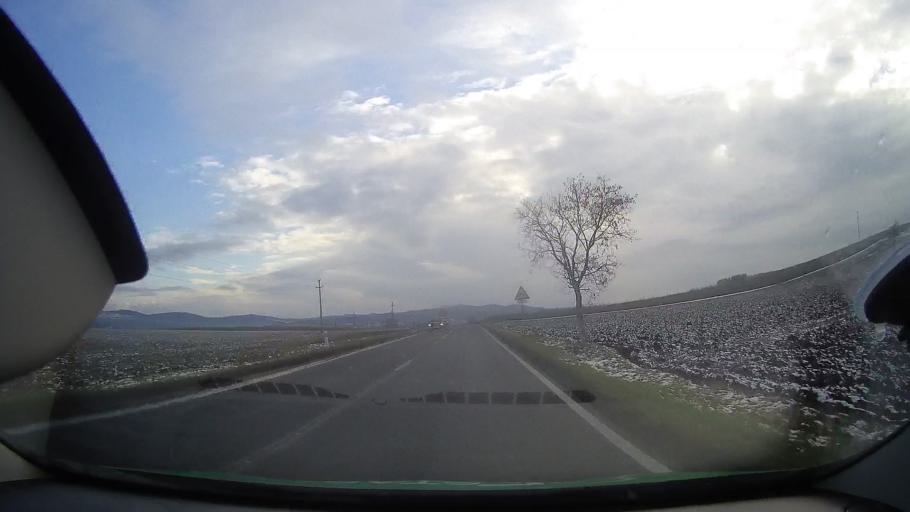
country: RO
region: Mures
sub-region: Comuna Cucerdea
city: Cucerdea
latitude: 46.4135
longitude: 24.2642
